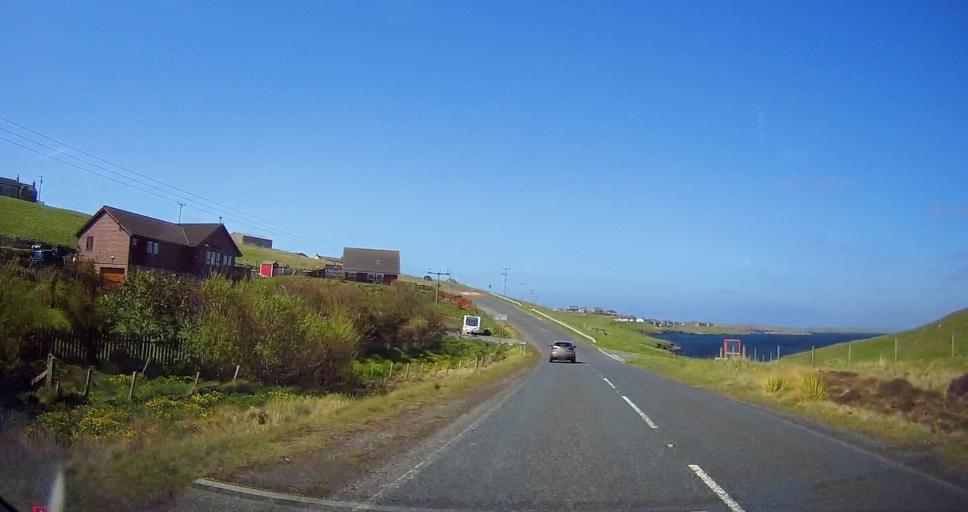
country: GB
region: Scotland
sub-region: Shetland Islands
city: Sandwick
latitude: 60.1047
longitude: -1.3184
